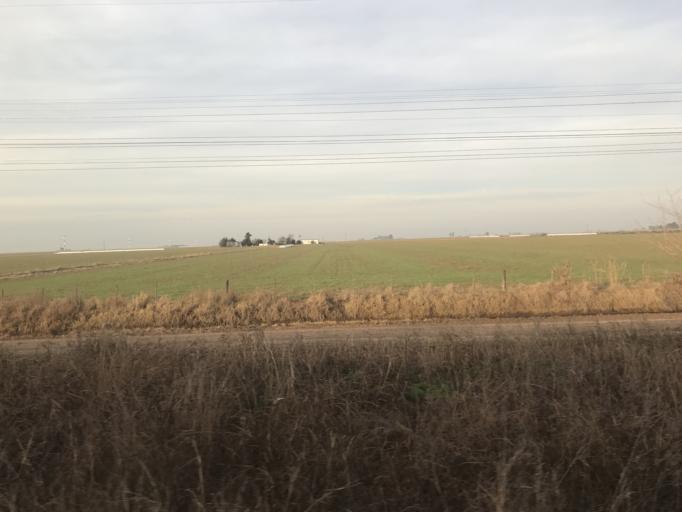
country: AR
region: Cordoba
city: Marcos Juarez
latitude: -32.6840
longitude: -62.1916
